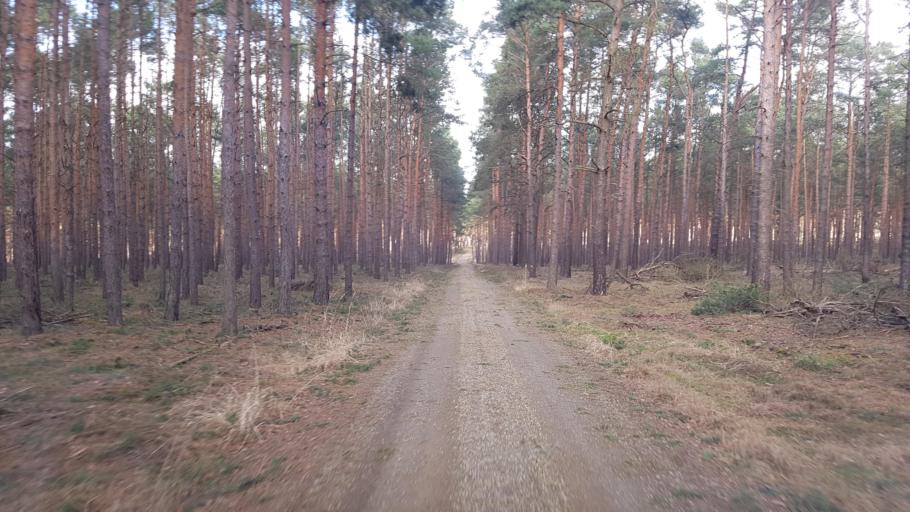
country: DE
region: Brandenburg
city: Schlieben
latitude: 51.6719
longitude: 13.3301
